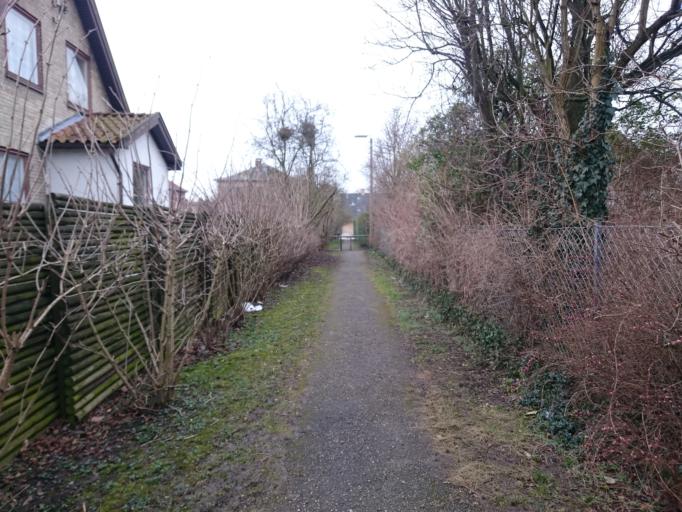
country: DK
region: Capital Region
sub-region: Kobenhavn
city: Vanlose
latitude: 55.6944
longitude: 12.5053
